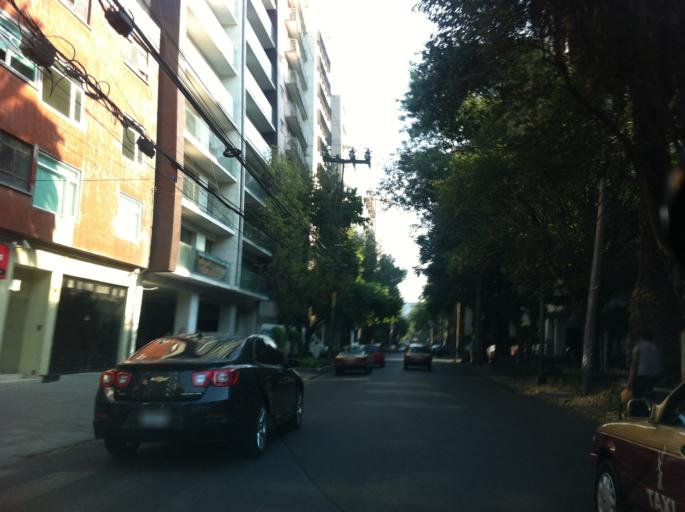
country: MX
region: Mexico City
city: Miguel Hidalgo
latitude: 19.4356
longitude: -99.1907
